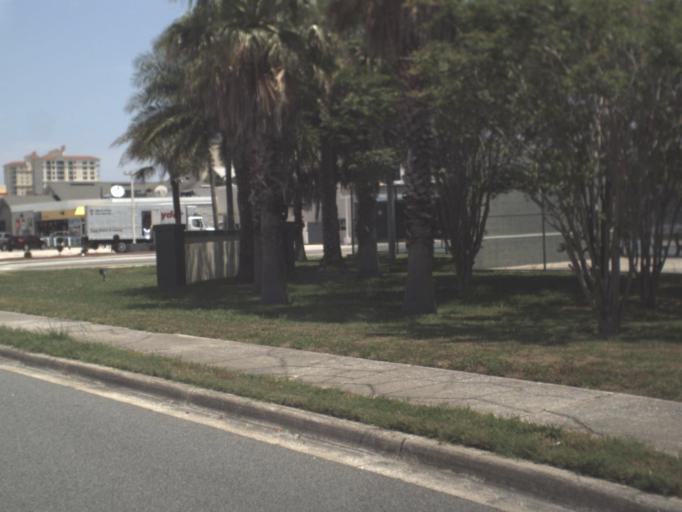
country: US
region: Florida
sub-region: Duval County
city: Jacksonville Beach
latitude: 30.2729
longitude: -81.3886
